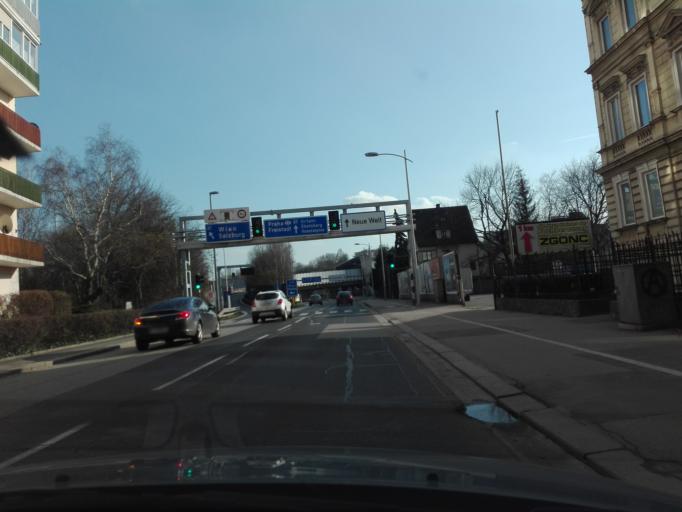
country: AT
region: Upper Austria
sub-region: Linz Stadt
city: Linz
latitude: 48.2840
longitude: 14.3022
